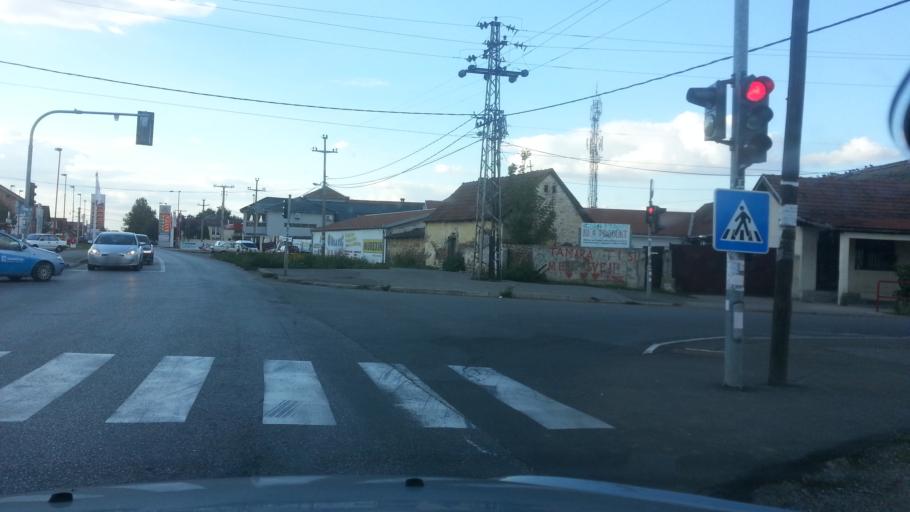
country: RS
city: Novi Banovci
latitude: 44.9122
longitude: 20.2644
